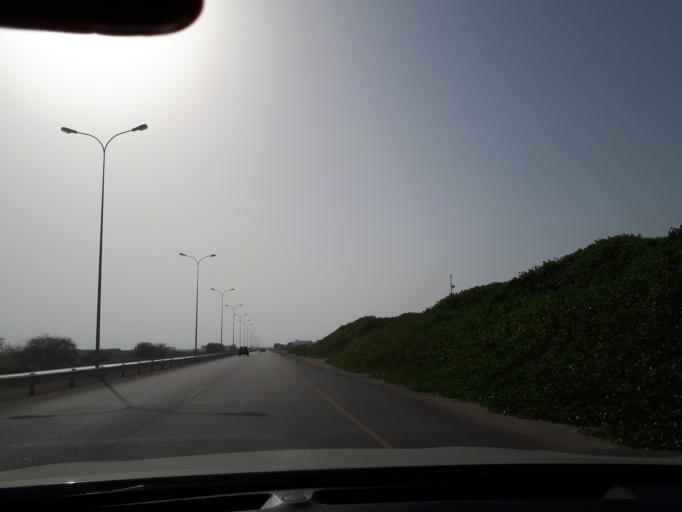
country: OM
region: Muhafazat Masqat
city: As Sib al Jadidah
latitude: 23.6163
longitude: 58.2867
